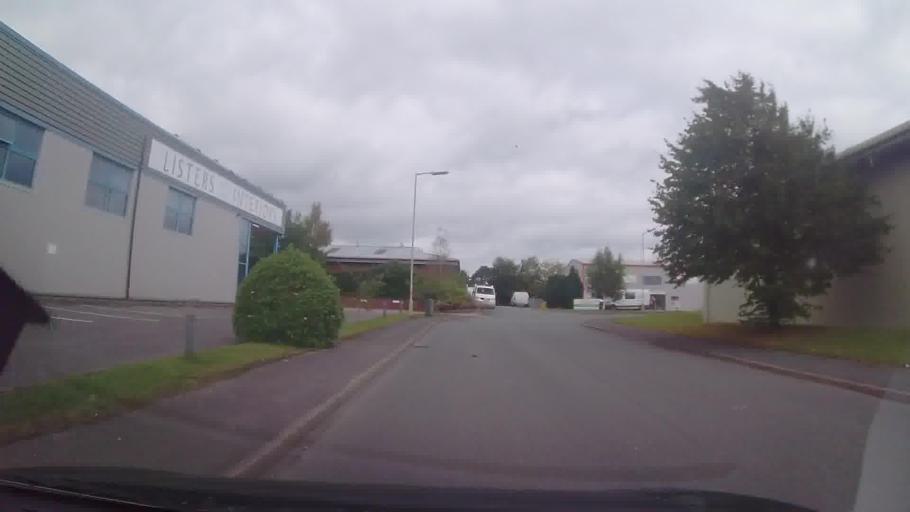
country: GB
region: England
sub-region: Shropshire
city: Whitchurch
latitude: 52.9654
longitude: -2.6687
